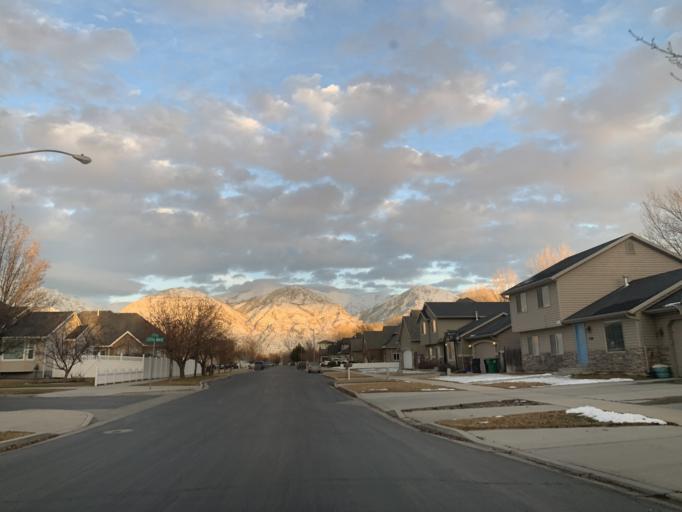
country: US
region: Utah
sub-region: Utah County
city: Provo
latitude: 40.2387
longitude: -111.7078
